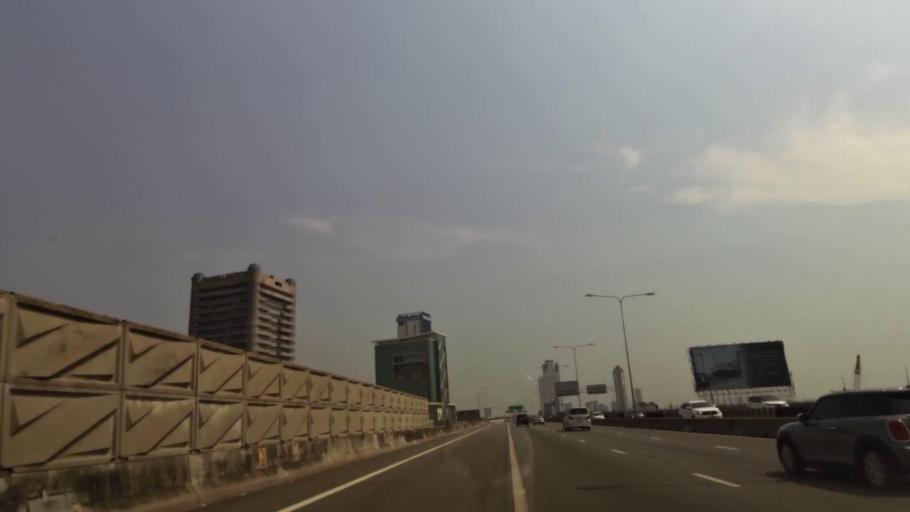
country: TH
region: Bangkok
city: Bang Na
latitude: 13.6674
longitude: 100.6393
